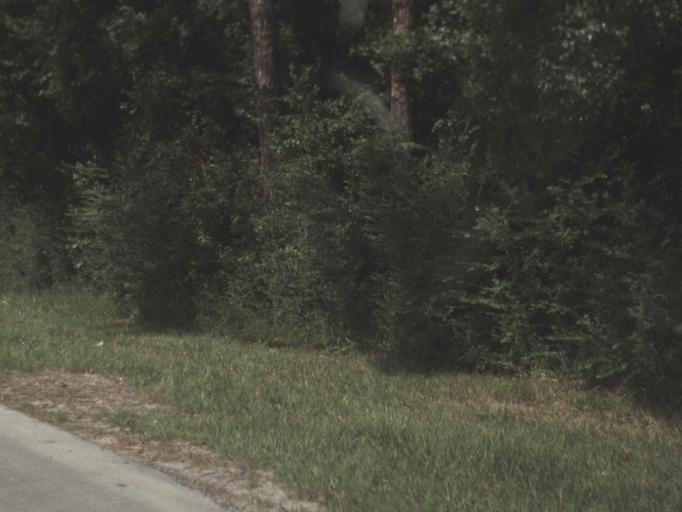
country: US
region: Florida
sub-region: Baker County
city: Macclenny
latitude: 30.2546
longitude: -82.1231
